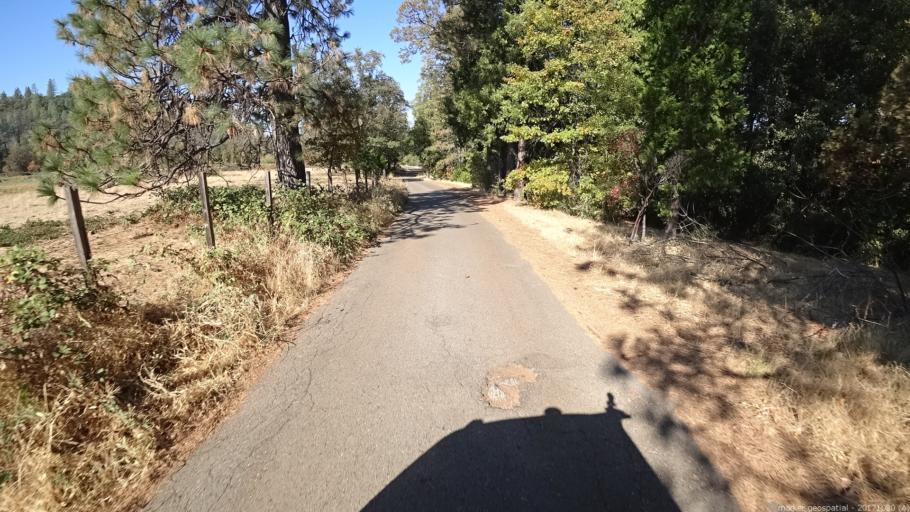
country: US
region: California
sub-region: Shasta County
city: Shingletown
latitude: 40.5258
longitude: -121.9234
